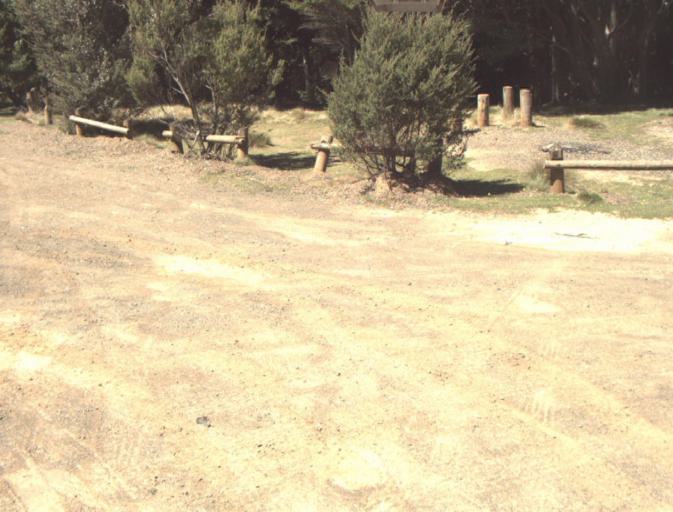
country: AU
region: Tasmania
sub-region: Dorset
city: Scottsdale
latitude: -41.3680
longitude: 147.4306
